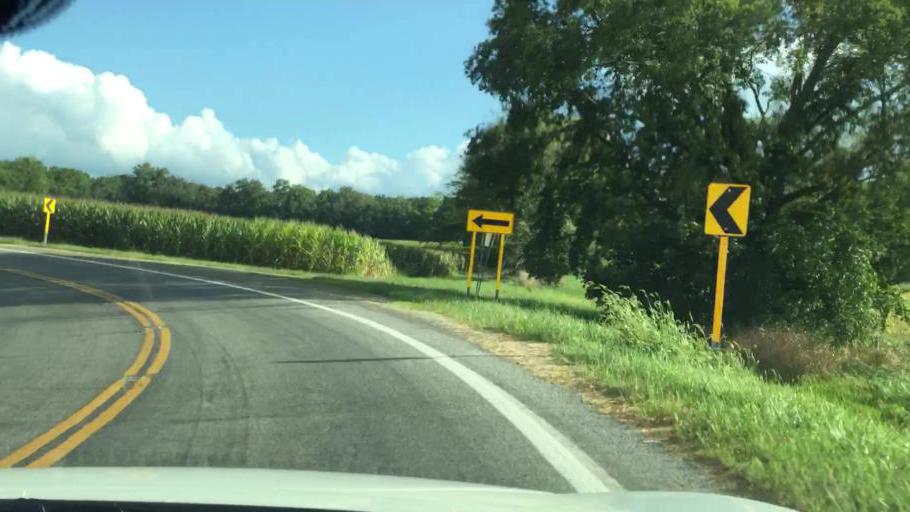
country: US
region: Ohio
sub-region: Champaign County
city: Mechanicsburg
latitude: 40.0421
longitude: -83.6077
